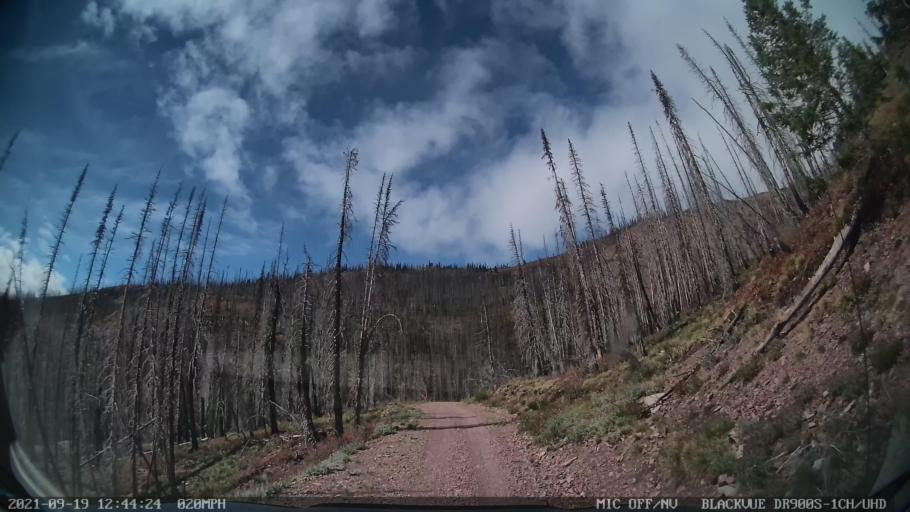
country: US
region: Montana
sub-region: Missoula County
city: Seeley Lake
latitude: 47.1904
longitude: -113.3491
